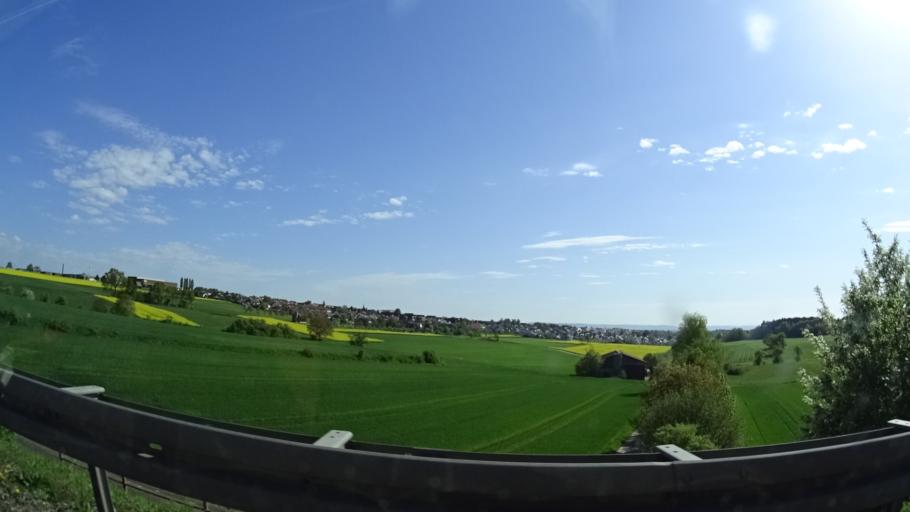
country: DE
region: Baden-Wuerttemberg
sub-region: Regierungsbezirk Stuttgart
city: Motzingen
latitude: 48.5264
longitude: 8.7628
